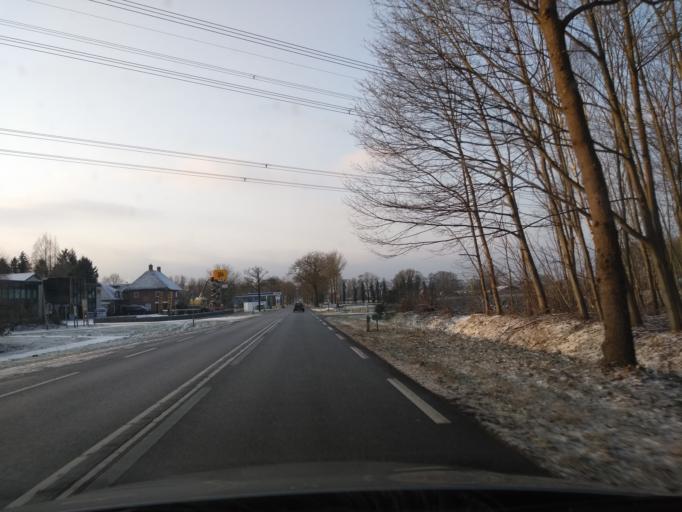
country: NL
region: Overijssel
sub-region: Gemeente Hof van Twente
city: Delden
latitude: 52.2459
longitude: 6.6956
